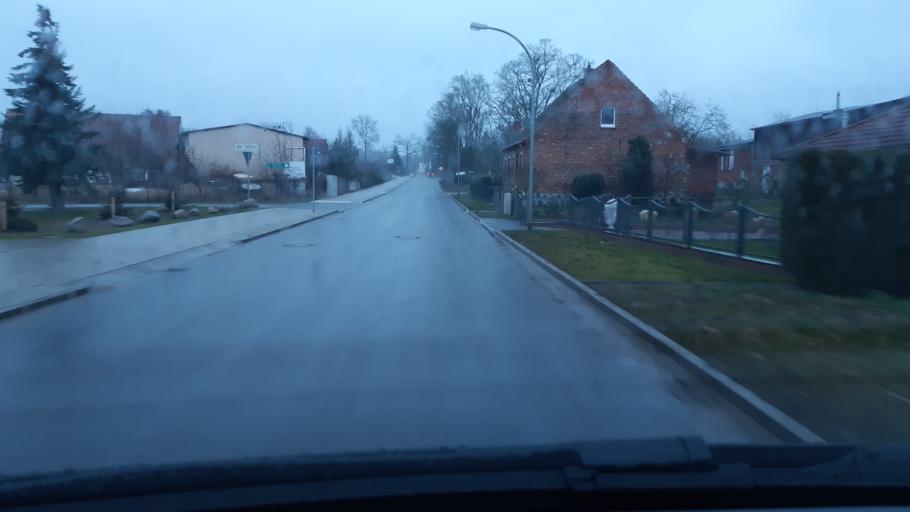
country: DE
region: Brandenburg
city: Milmersdorf
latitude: 53.1125
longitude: 13.6413
